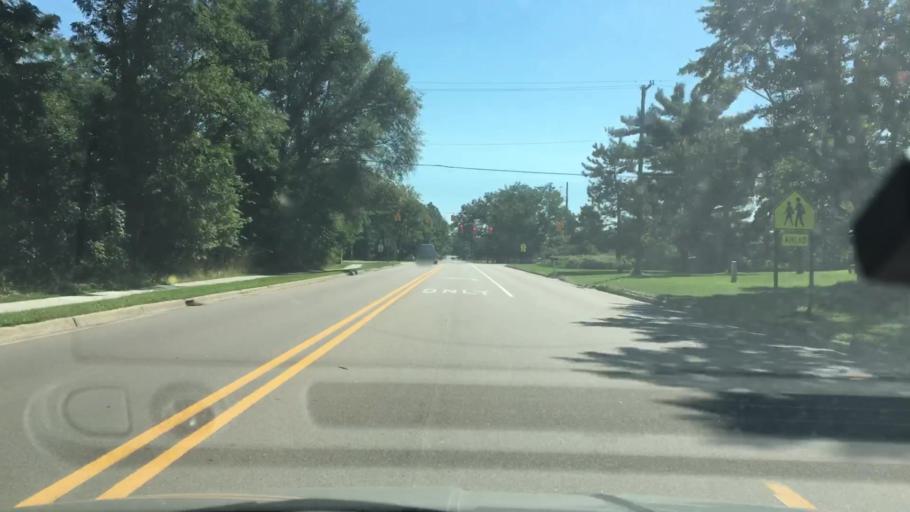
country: US
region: Michigan
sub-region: Livingston County
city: Brighton
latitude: 42.5088
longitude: -83.7689
